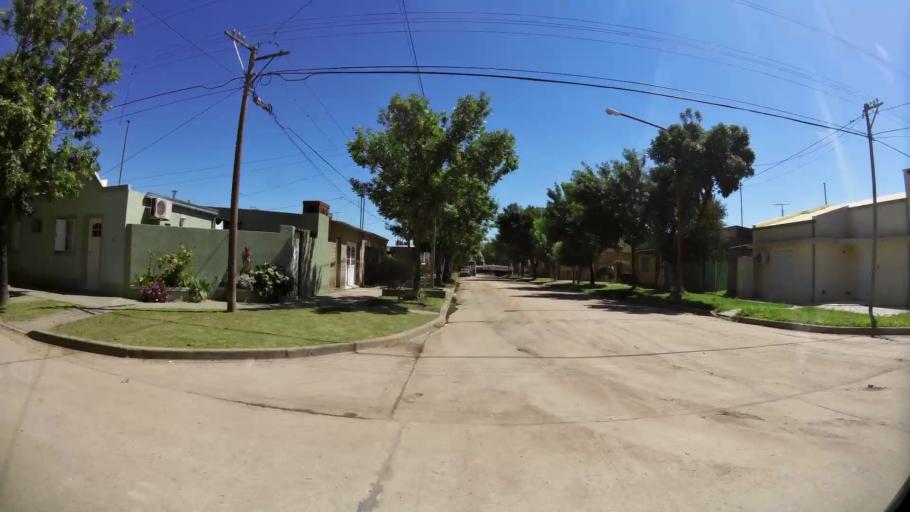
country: AR
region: Santa Fe
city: Esperanza
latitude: -31.4372
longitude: -60.9296
